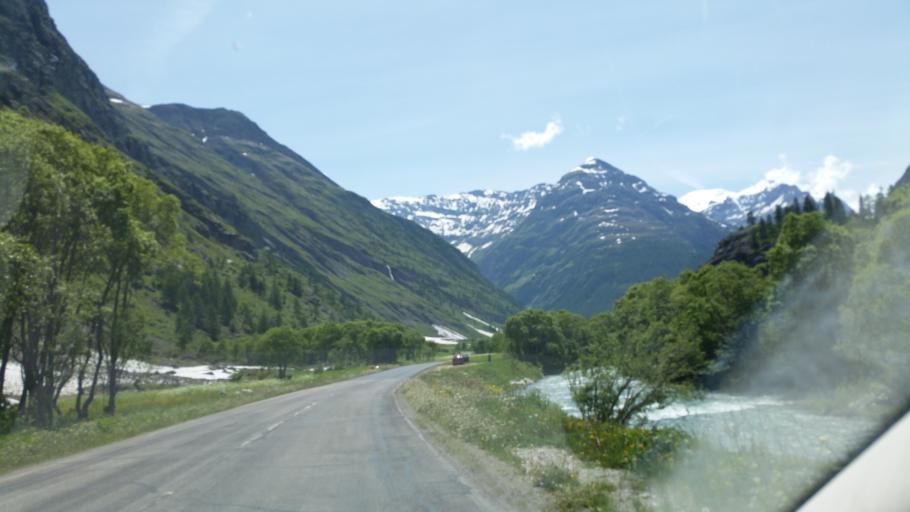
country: FR
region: Rhone-Alpes
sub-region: Departement de la Savoie
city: Val-d'Isere
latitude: 45.3524
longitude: 7.0302
